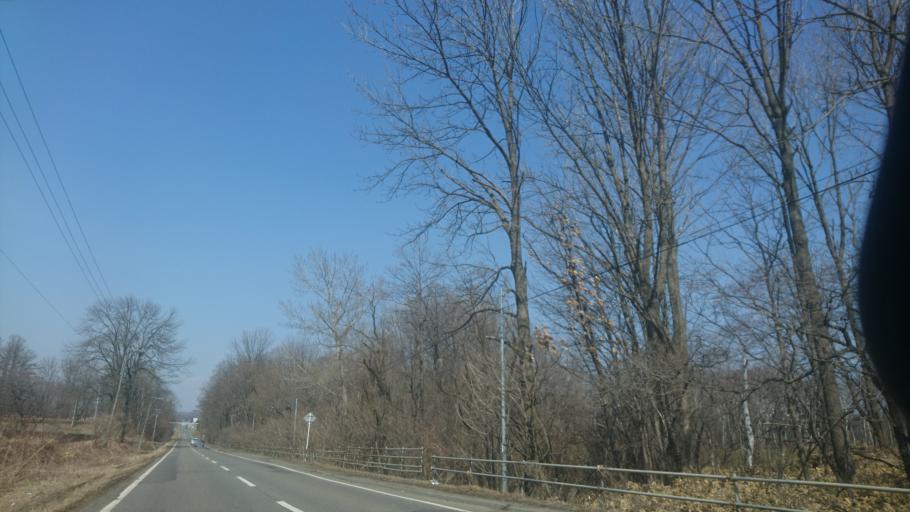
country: JP
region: Hokkaido
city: Obihiro
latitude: 42.9159
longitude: 143.0832
